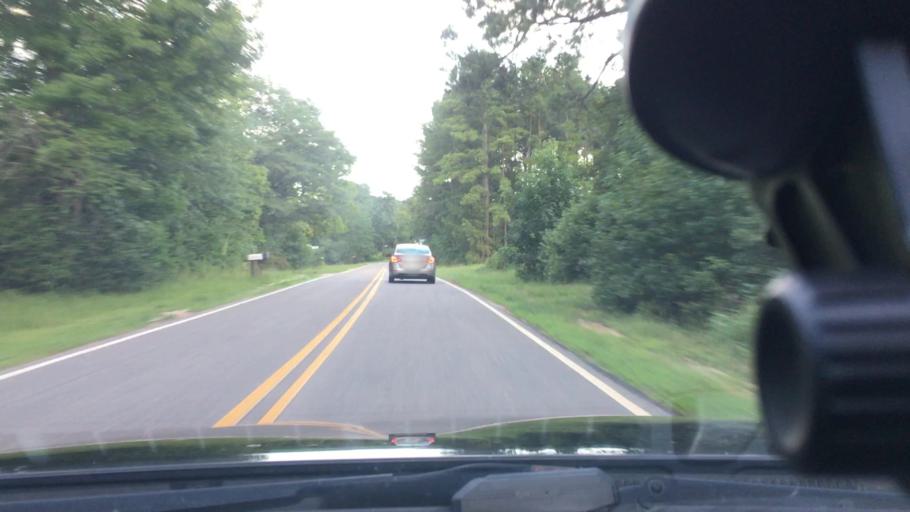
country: US
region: North Carolina
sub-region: Moore County
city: Carthage
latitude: 35.3619
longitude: -79.3288
